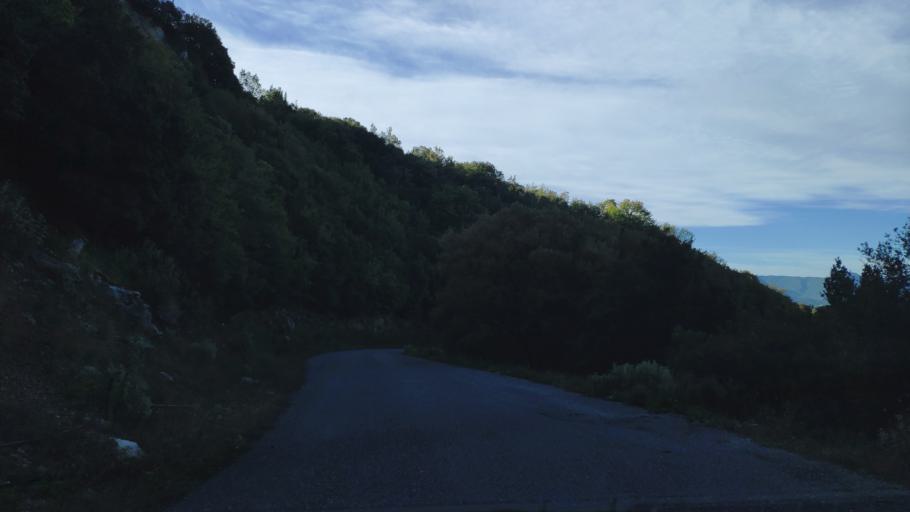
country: GR
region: Peloponnese
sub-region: Nomos Arkadias
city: Dimitsana
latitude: 37.5496
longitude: 22.0601
